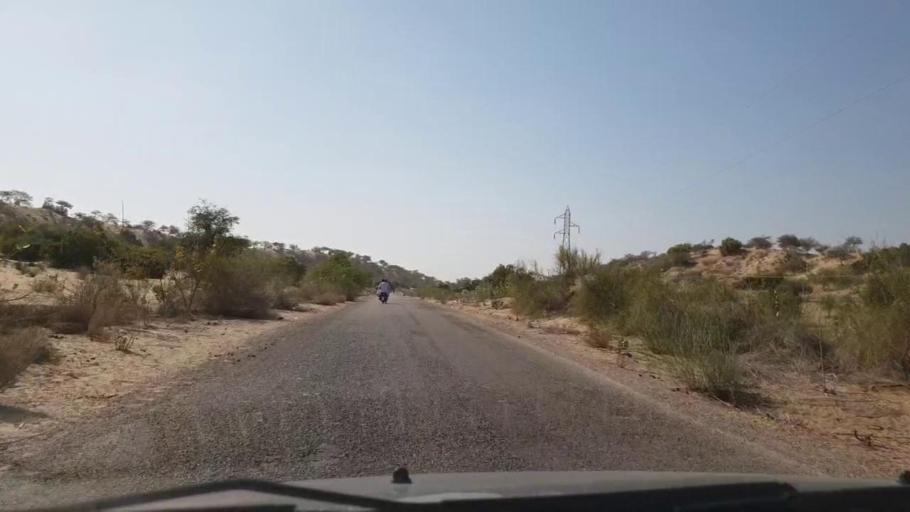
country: PK
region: Sindh
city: Diplo
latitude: 24.5783
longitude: 69.6968
